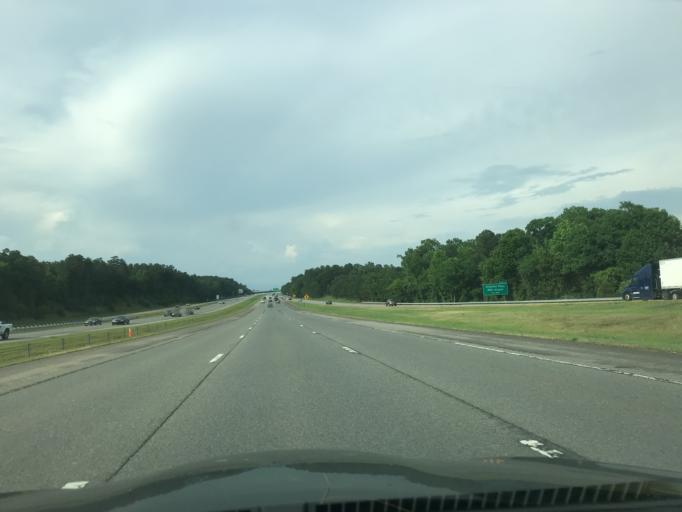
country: US
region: North Carolina
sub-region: Wake County
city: Morrisville
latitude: 35.8759
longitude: -78.8281
